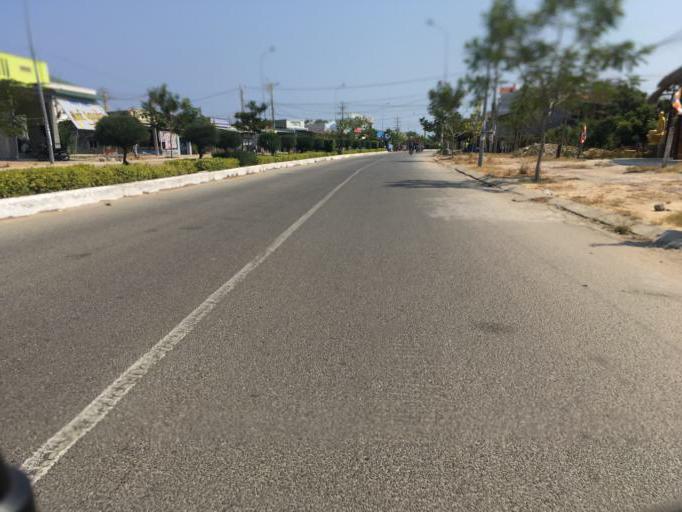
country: VN
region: Ninh Thuan
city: Phan Rang-Thap Cham
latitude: 11.5531
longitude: 109.0244
